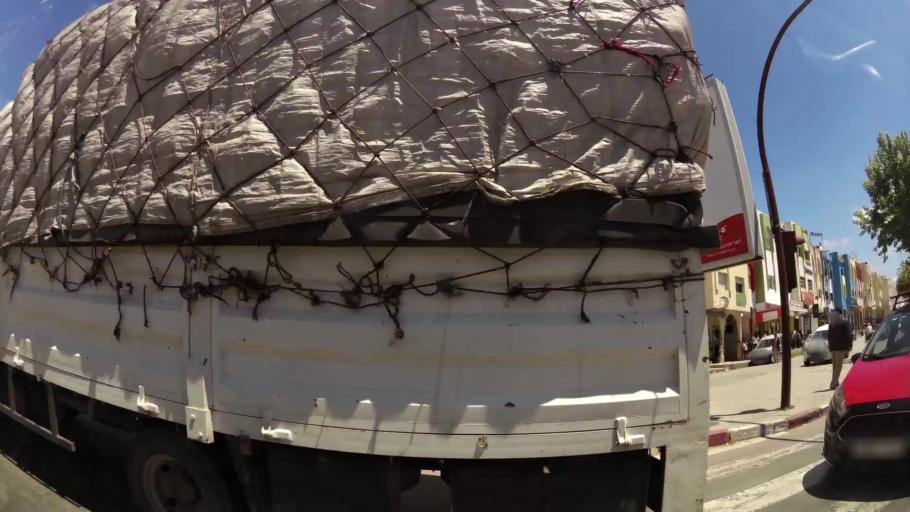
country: MA
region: Fes-Boulemane
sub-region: Fes
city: Fes
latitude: 34.0134
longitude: -4.9820
